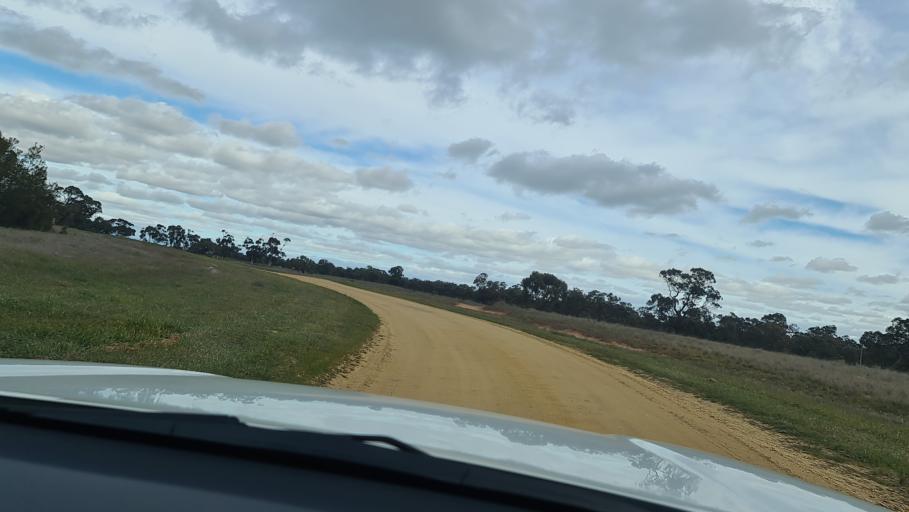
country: AU
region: Victoria
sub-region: Horsham
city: Horsham
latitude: -36.6204
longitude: 142.4204
